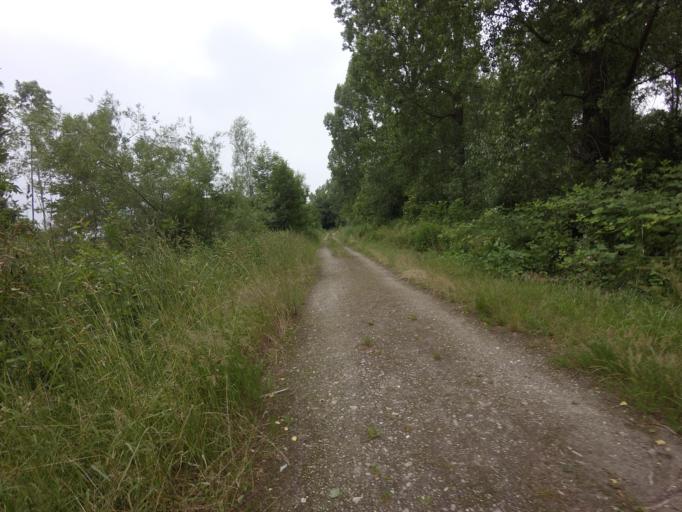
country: NL
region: Flevoland
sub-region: Gemeente Almere
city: Almere Stad
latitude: 52.4064
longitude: 5.3351
